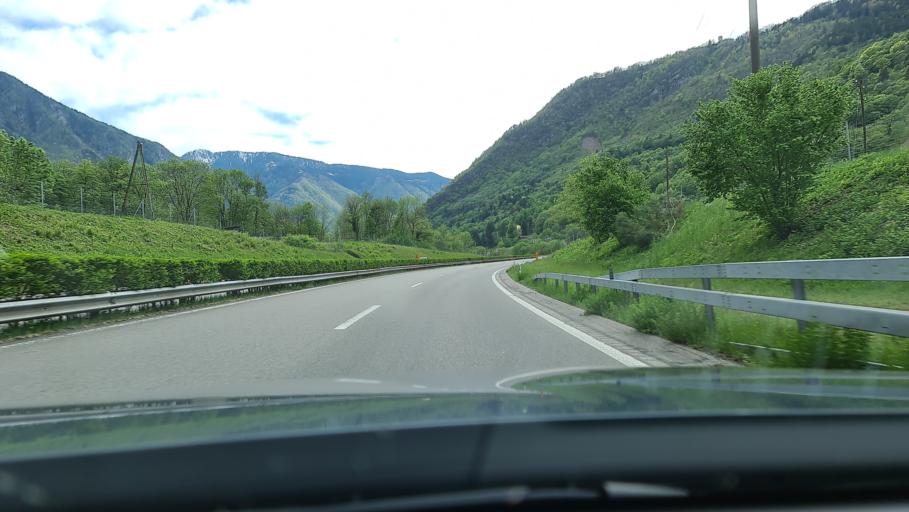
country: CH
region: Grisons
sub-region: Moesa District
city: Santa Maria in Calanca
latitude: 46.2705
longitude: 9.1737
